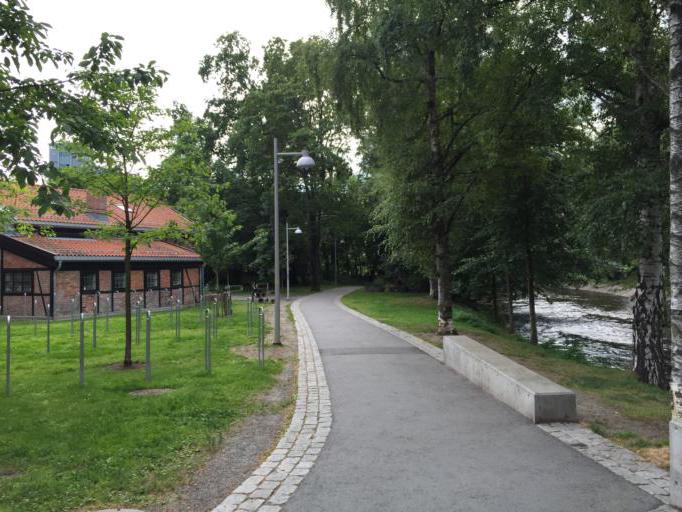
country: NO
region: Oslo
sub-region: Oslo
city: Oslo
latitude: 59.9254
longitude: 10.7537
